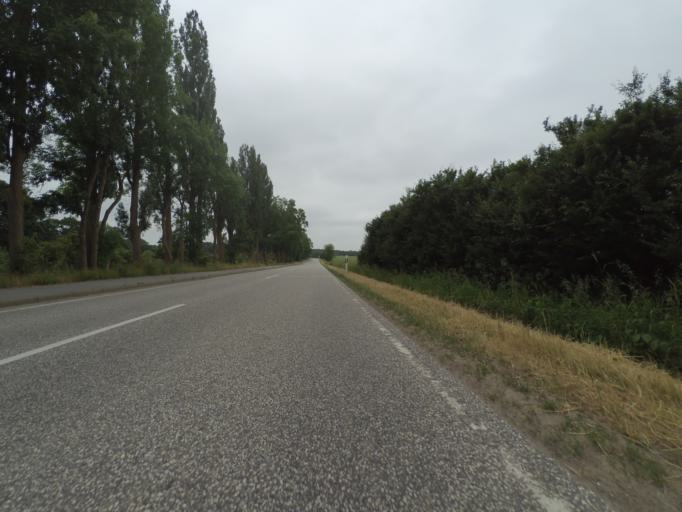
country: DE
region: Mecklenburg-Vorpommern
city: Goldberg
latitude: 53.5484
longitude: 12.0613
